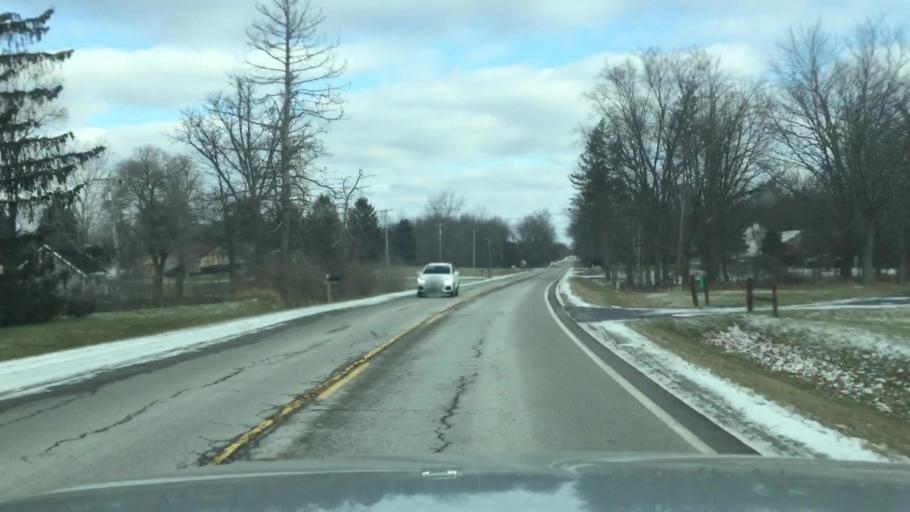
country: US
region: Michigan
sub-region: Genesee County
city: Linden
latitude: 42.8511
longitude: -83.7825
